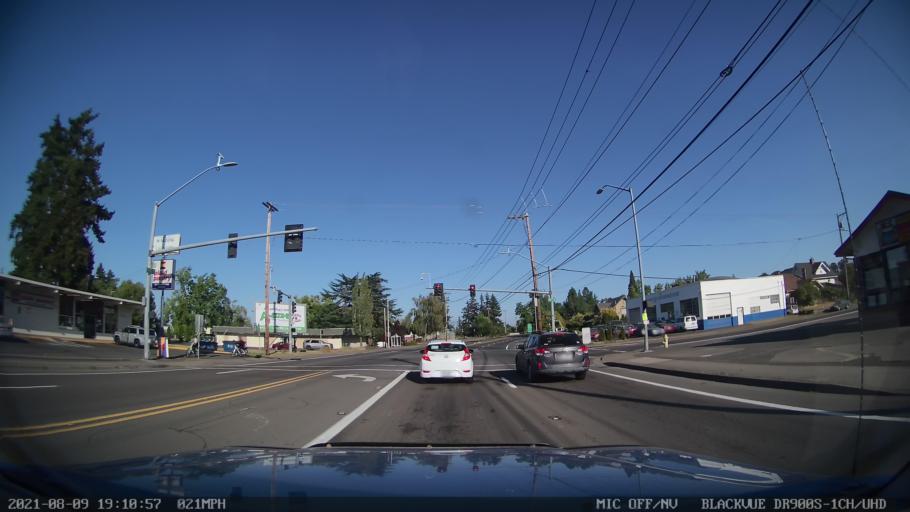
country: US
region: Oregon
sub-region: Marion County
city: Four Corners
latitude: 44.9325
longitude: -123.0102
